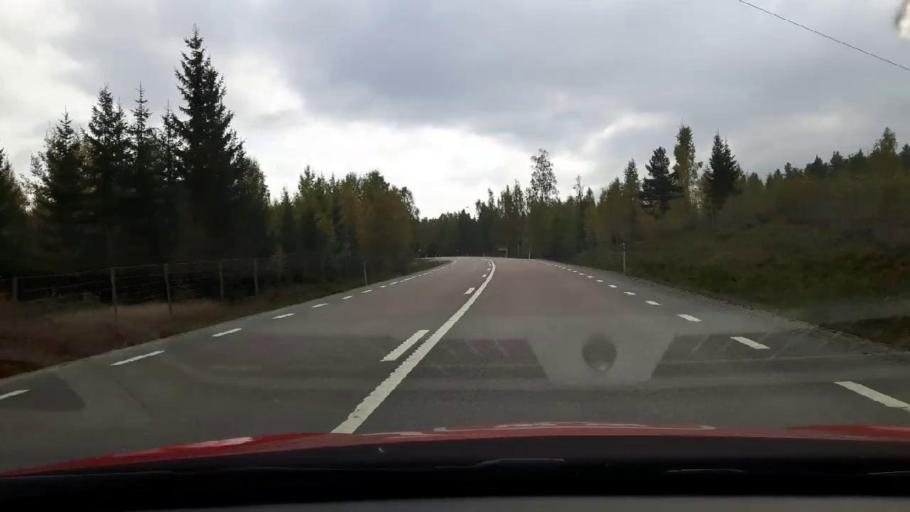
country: SE
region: Gaevleborg
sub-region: Bollnas Kommun
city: Kilafors
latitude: 61.2768
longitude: 16.5244
